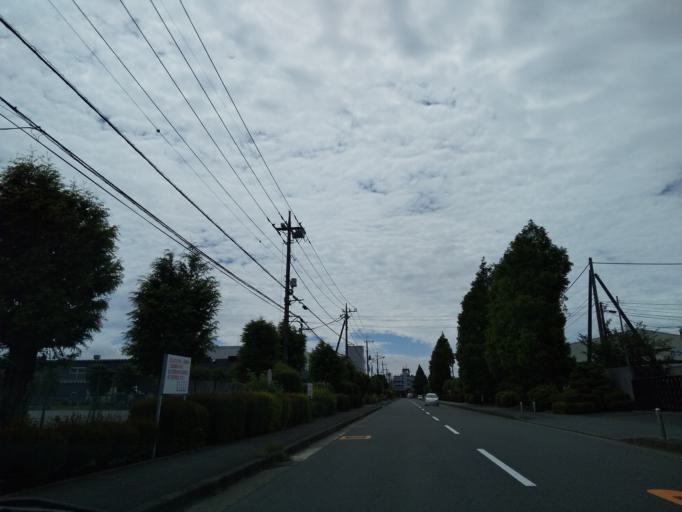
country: JP
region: Kanagawa
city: Zama
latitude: 35.5133
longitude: 139.3539
